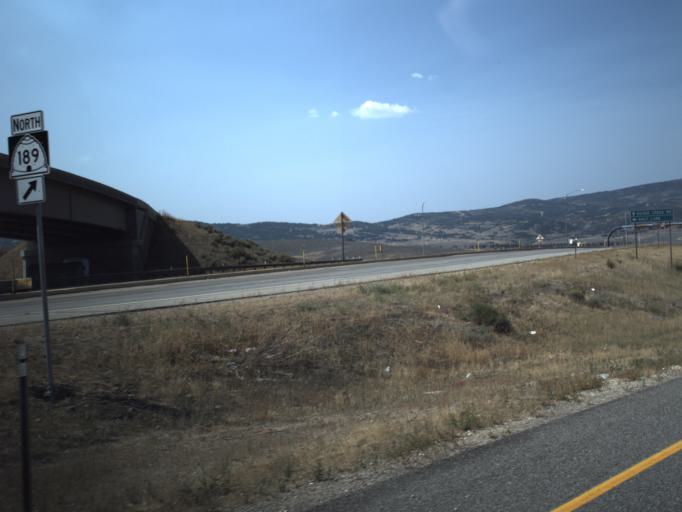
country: US
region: Utah
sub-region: Summit County
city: Snyderville
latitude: 40.7298
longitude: -111.4958
